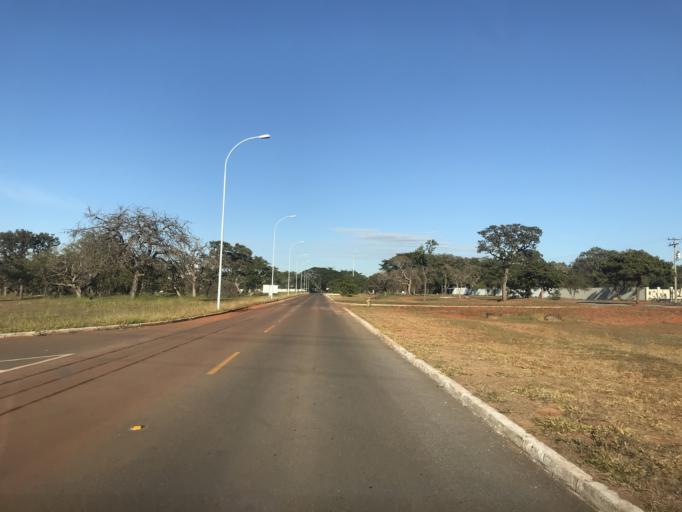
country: BR
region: Federal District
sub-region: Brasilia
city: Brasilia
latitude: -15.8270
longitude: -47.8941
